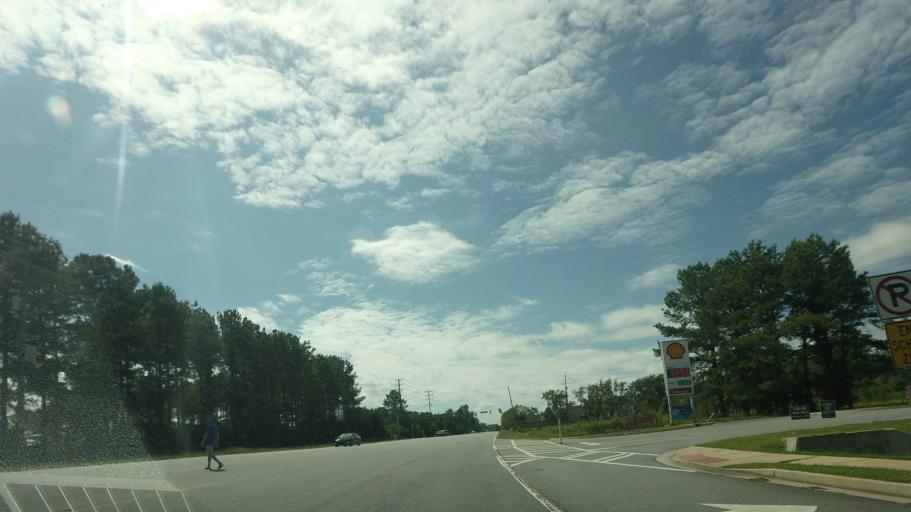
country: US
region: Georgia
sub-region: Houston County
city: Centerville
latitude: 32.5720
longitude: -83.6913
